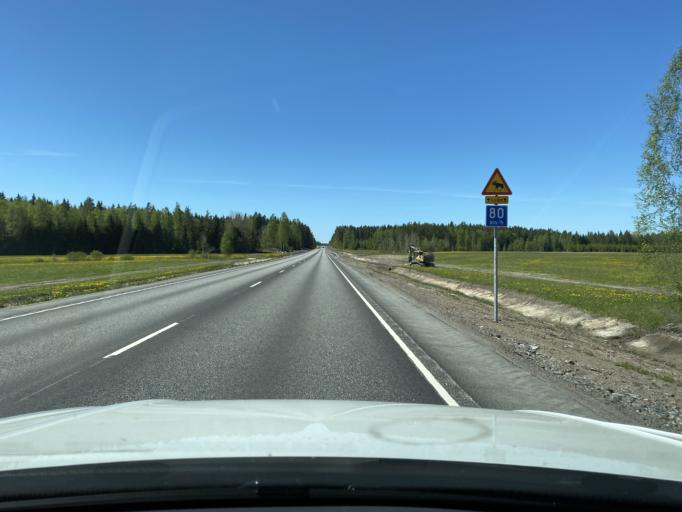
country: FI
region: Satakunta
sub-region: Rauma
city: Koeylioe
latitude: 61.1649
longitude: 22.3612
